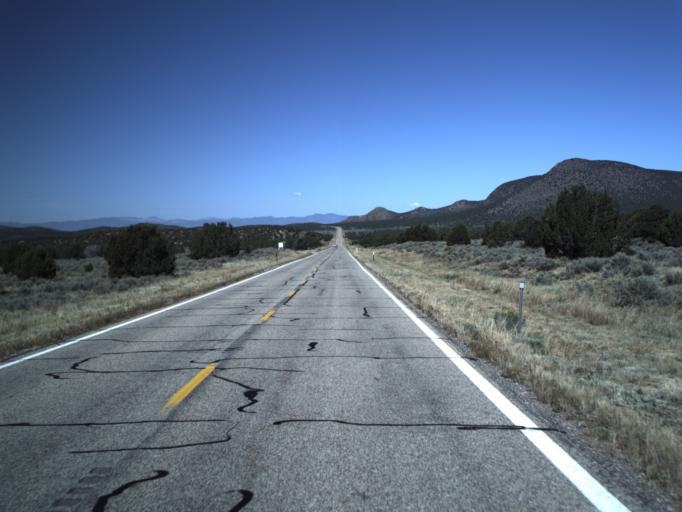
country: US
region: Utah
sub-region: Washington County
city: Enterprise
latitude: 37.6315
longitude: -113.4273
